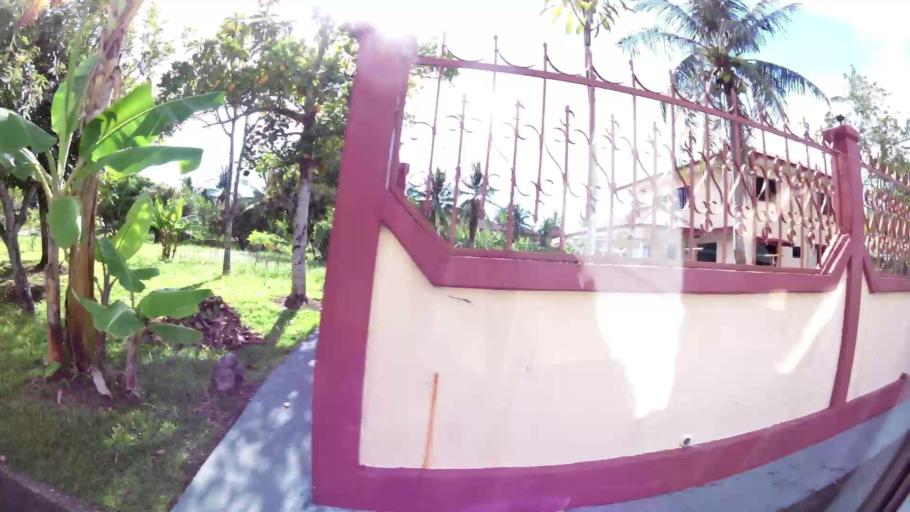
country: BN
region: Brunei and Muara
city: Bandar Seri Begawan
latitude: 4.9865
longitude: 115.0233
